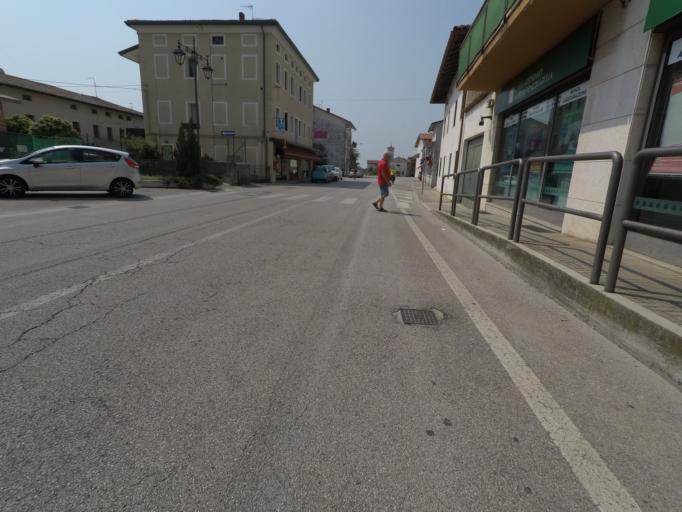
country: IT
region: Friuli Venezia Giulia
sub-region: Provincia di Pordenone
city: Montereale Valcellina
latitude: 46.1585
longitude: 12.6608
